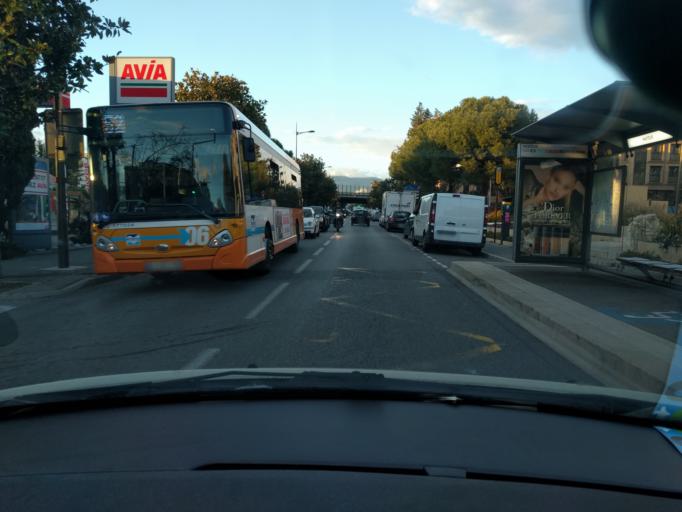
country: FR
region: Provence-Alpes-Cote d'Azur
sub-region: Departement des Alpes-Maritimes
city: Saint-Laurent-du-Var
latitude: 43.6654
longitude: 7.1934
